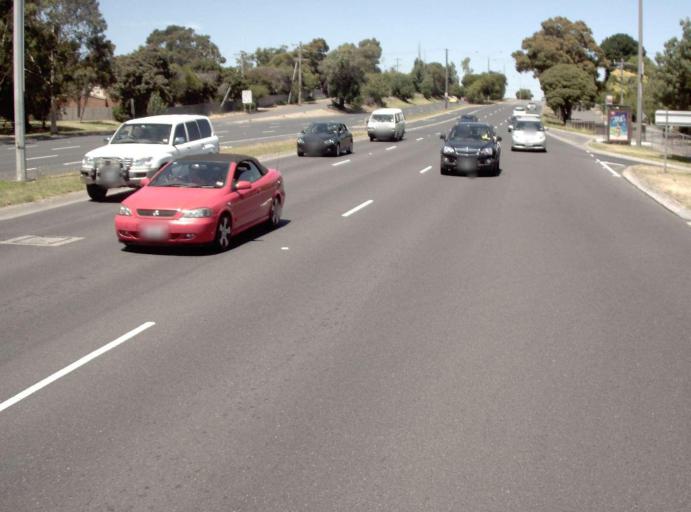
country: AU
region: Victoria
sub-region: Monash
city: Clayton
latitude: -37.9152
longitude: 145.1281
